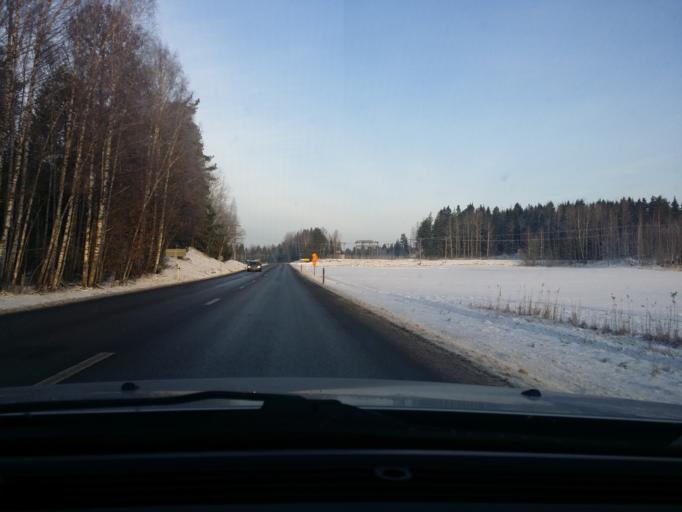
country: SE
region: OErebro
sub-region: Lindesbergs Kommun
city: Frovi
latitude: 59.5003
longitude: 15.3753
